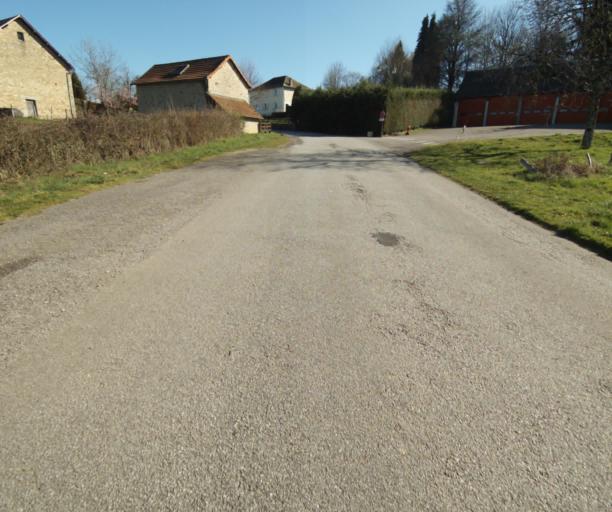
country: FR
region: Limousin
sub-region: Departement de la Correze
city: Chamboulive
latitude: 45.4671
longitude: 1.7310
